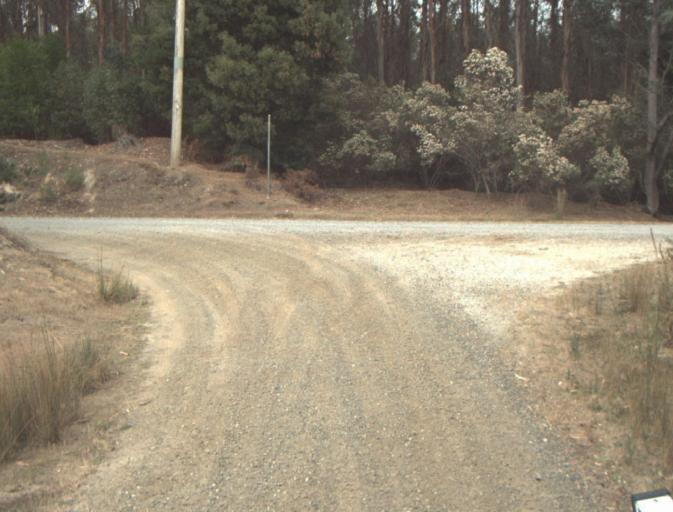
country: AU
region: Tasmania
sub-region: Launceston
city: Mayfield
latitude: -41.1523
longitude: 147.1732
